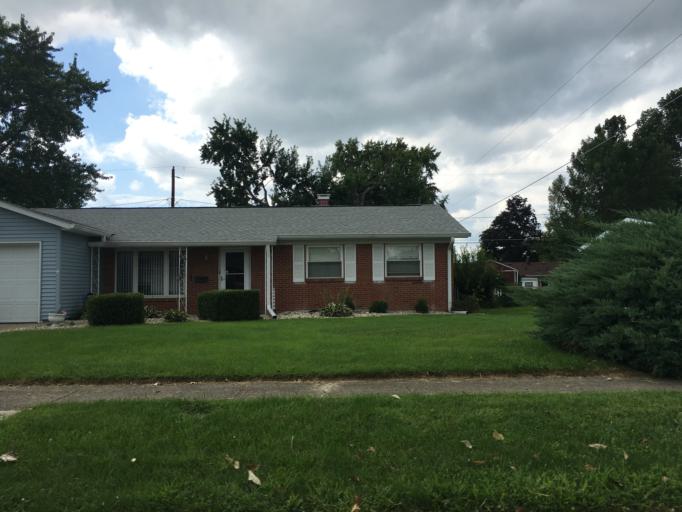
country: US
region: Indiana
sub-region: Howard County
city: Kokomo
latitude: 40.4667
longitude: -86.1034
